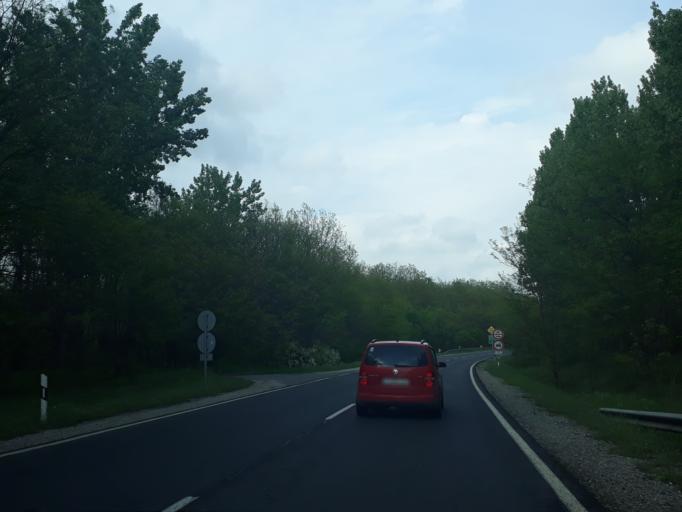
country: HU
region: Szabolcs-Szatmar-Bereg
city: Nyirbogdany
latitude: 48.0534
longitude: 21.9039
